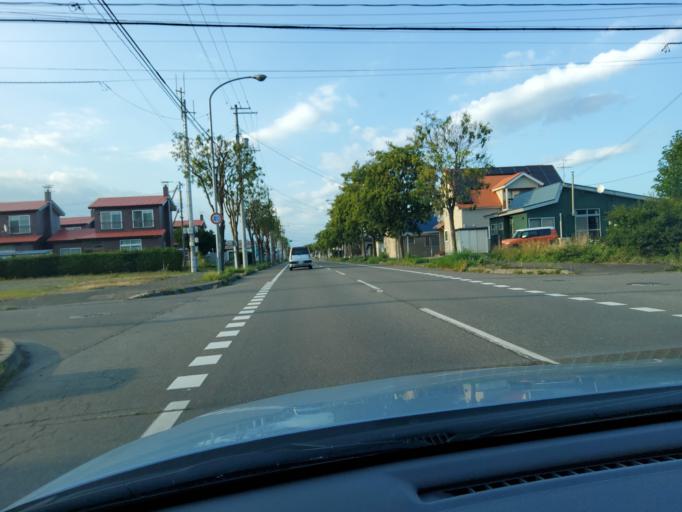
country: JP
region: Hokkaido
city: Obihiro
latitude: 42.9369
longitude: 143.1842
